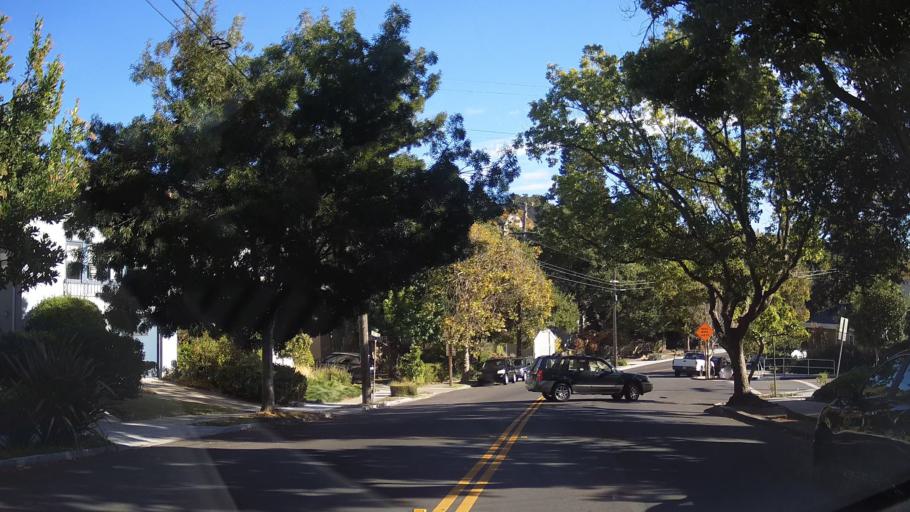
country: US
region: California
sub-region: Contra Costa County
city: Kensington
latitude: 37.8946
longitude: -122.2773
